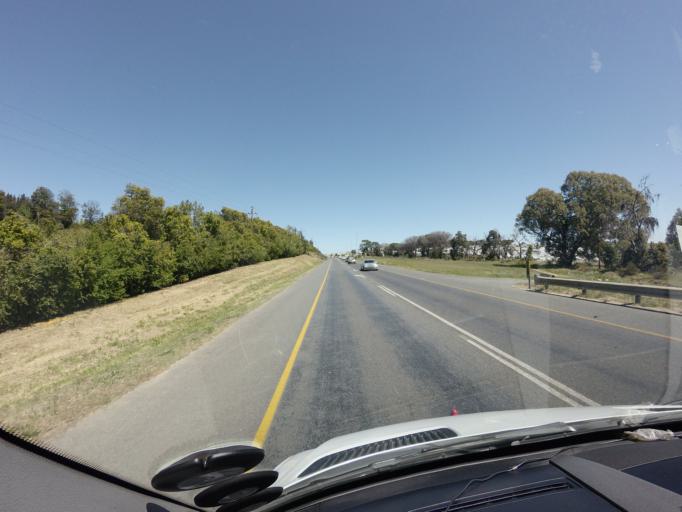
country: ZA
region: Western Cape
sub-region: Cape Winelands District Municipality
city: Stellenbosch
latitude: -33.8969
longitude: 18.8593
